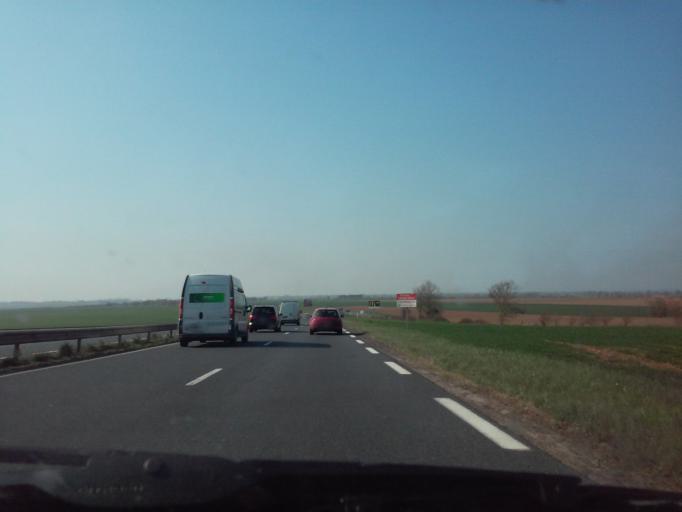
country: FR
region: Lower Normandy
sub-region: Departement du Calvados
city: Tilly-sur-Seulles
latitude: 49.2422
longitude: -0.6063
